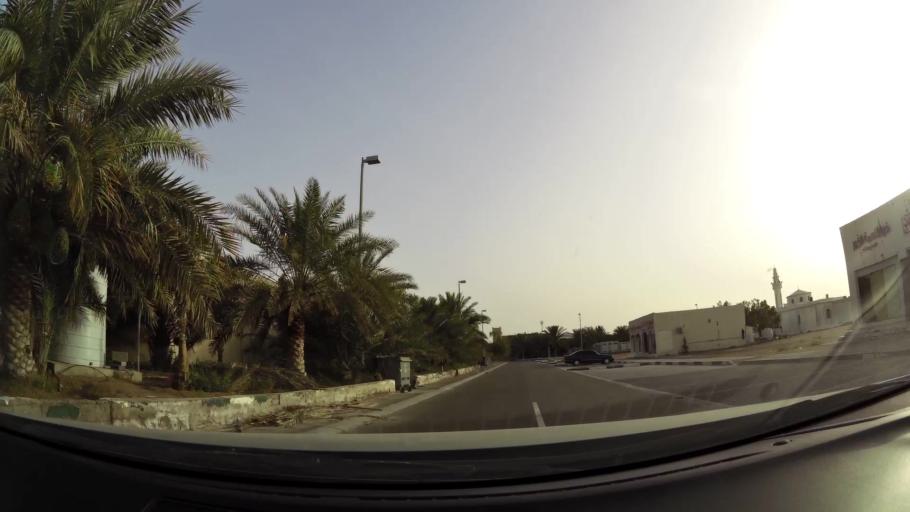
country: AE
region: Abu Dhabi
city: Al Ain
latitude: 24.1078
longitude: 55.7079
